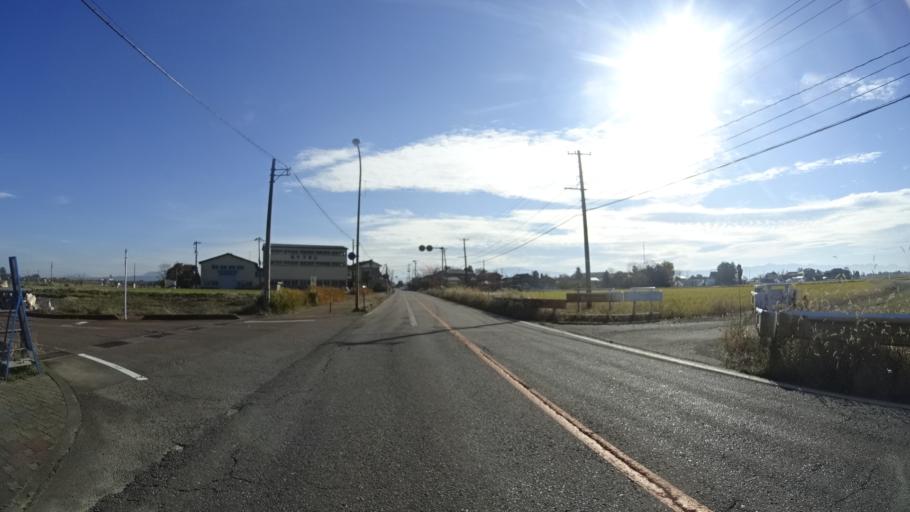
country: JP
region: Niigata
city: Mitsuke
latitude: 37.5523
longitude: 138.8642
